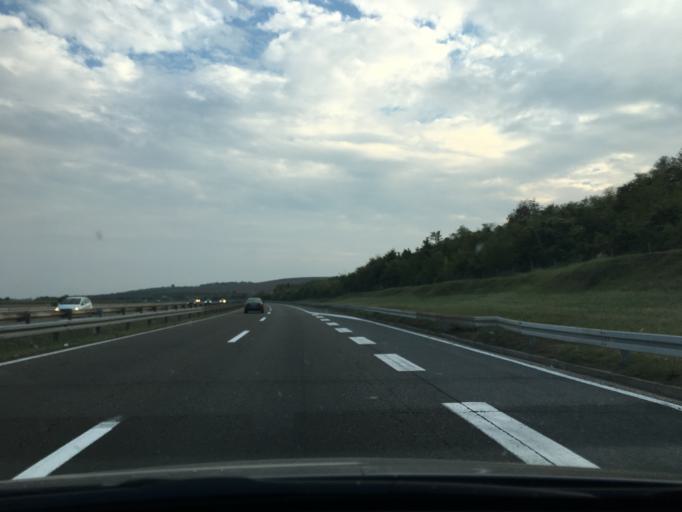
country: RS
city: Lugavcina
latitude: 44.4657
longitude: 21.0380
